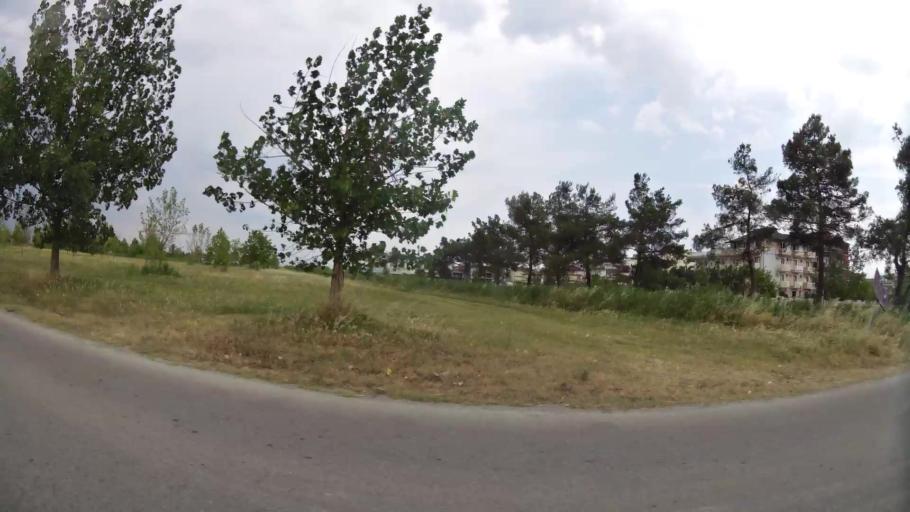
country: GR
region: Central Macedonia
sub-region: Nomos Pierias
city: Paralia
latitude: 40.2739
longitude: 22.5958
